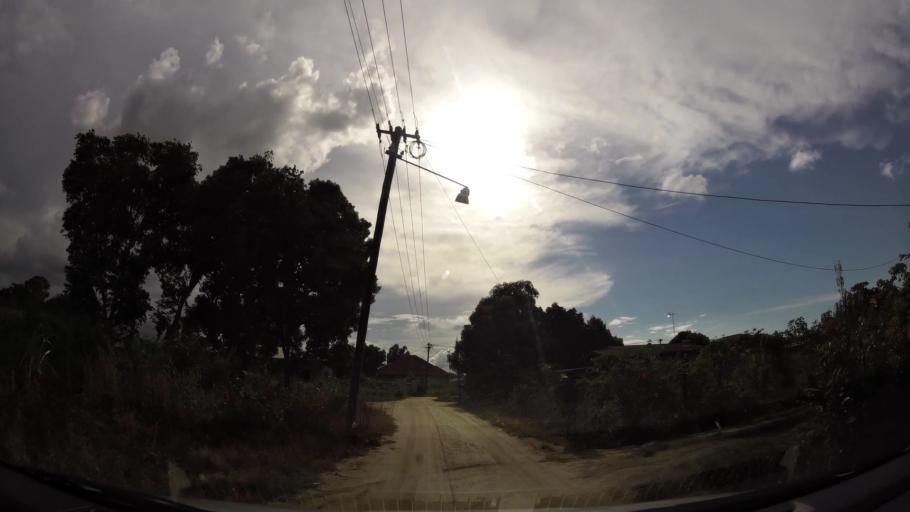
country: SR
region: Paramaribo
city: Paramaribo
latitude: 5.8461
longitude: -55.1832
